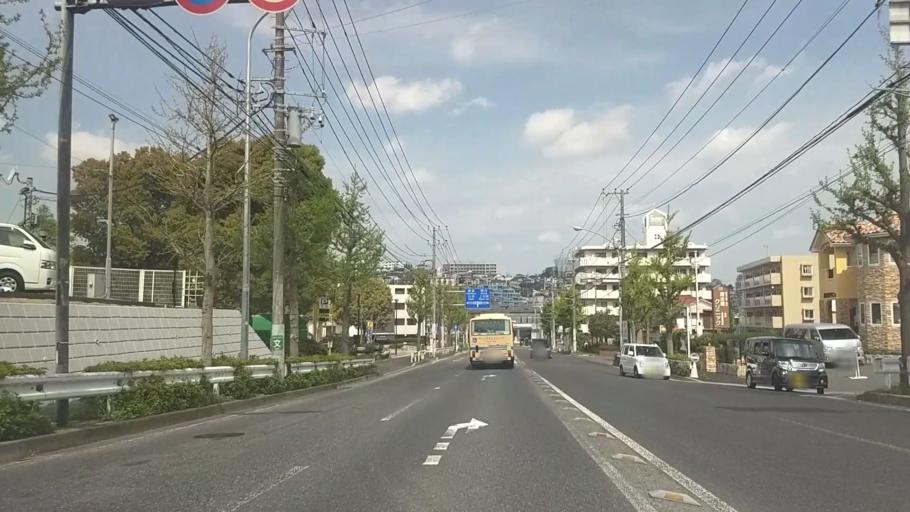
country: JP
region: Kanagawa
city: Yokohama
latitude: 35.3890
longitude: 139.5838
